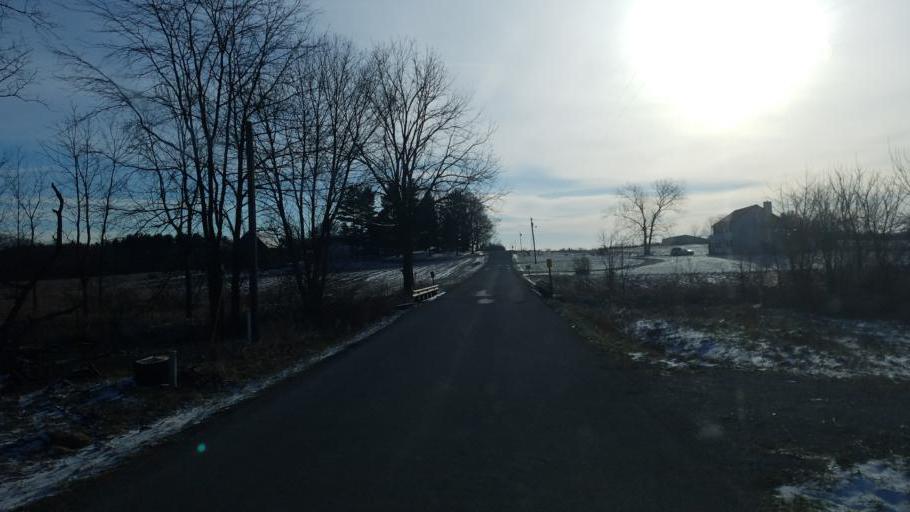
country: US
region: Ohio
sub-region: Morrow County
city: Mount Gilead
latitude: 40.6251
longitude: -82.8108
